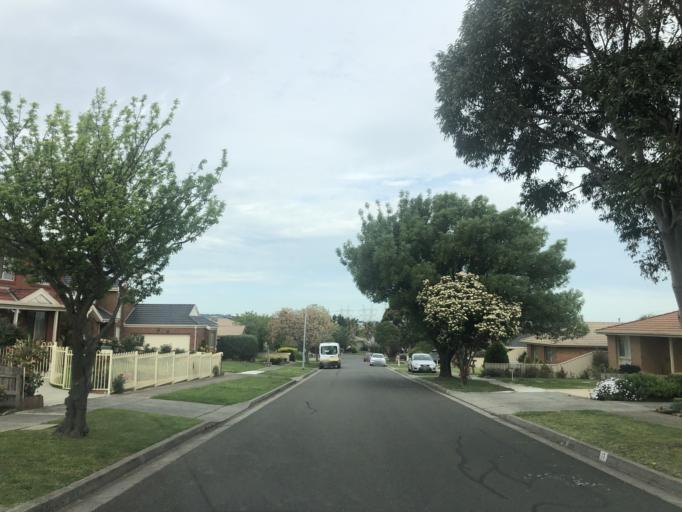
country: AU
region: Victoria
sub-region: Casey
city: Hallam
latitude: -38.0103
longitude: 145.2789
